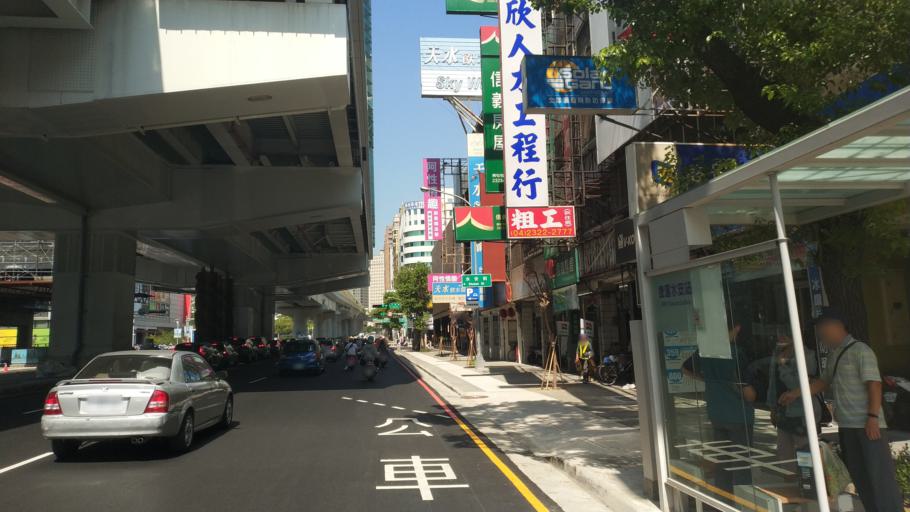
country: TW
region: Taiwan
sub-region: Taichung City
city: Taichung
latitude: 24.1527
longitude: 120.6469
